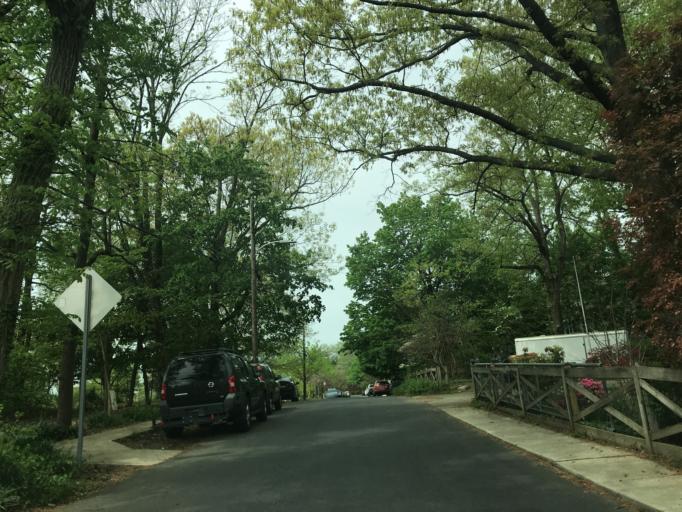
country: US
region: Maryland
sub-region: Baltimore County
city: Catonsville
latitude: 39.2715
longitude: -76.7461
